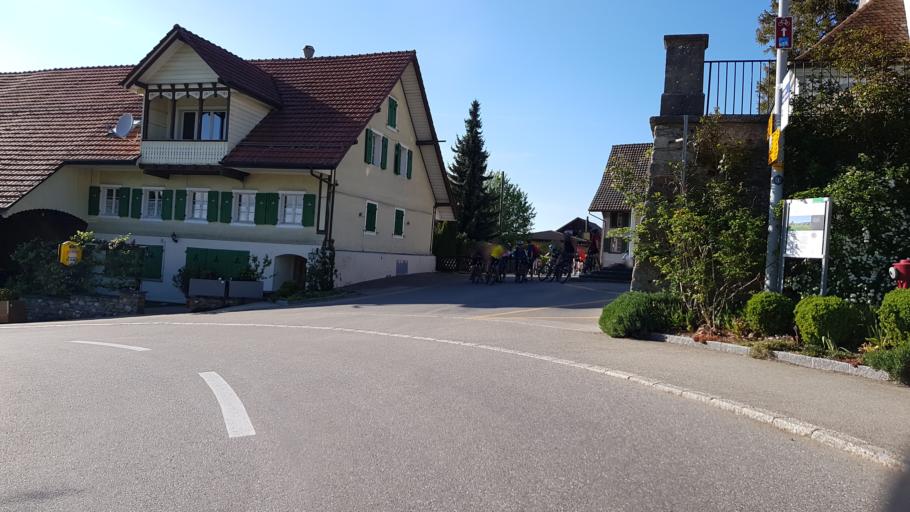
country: CH
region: Aargau
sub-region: Bezirk Muri
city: Buttwil
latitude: 47.2727
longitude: 8.2775
